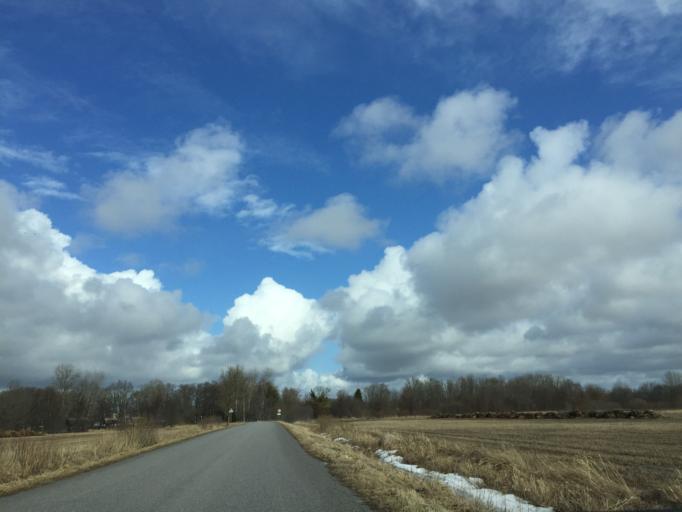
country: EE
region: Laeaene
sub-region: Lihula vald
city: Lihula
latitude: 58.7111
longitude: 23.8135
